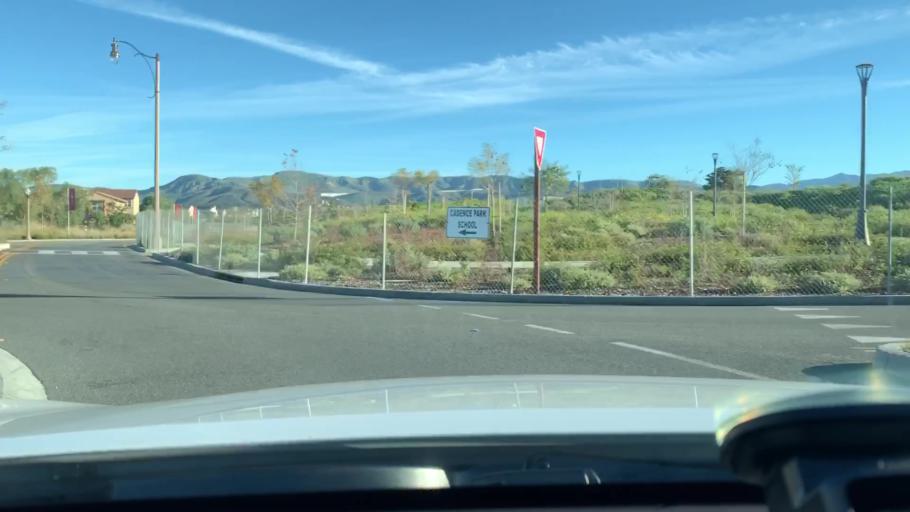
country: US
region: California
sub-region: Orange County
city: Lake Forest
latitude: 33.6826
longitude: -117.7320
